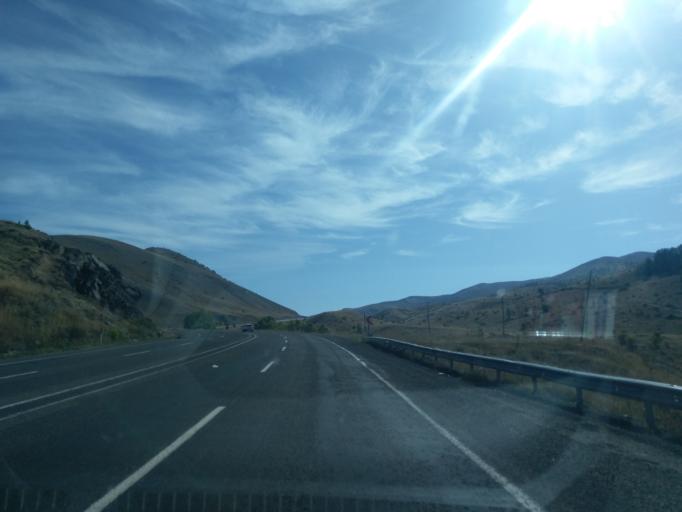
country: TR
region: Sivas
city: Akincilar
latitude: 39.8561
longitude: 38.3570
